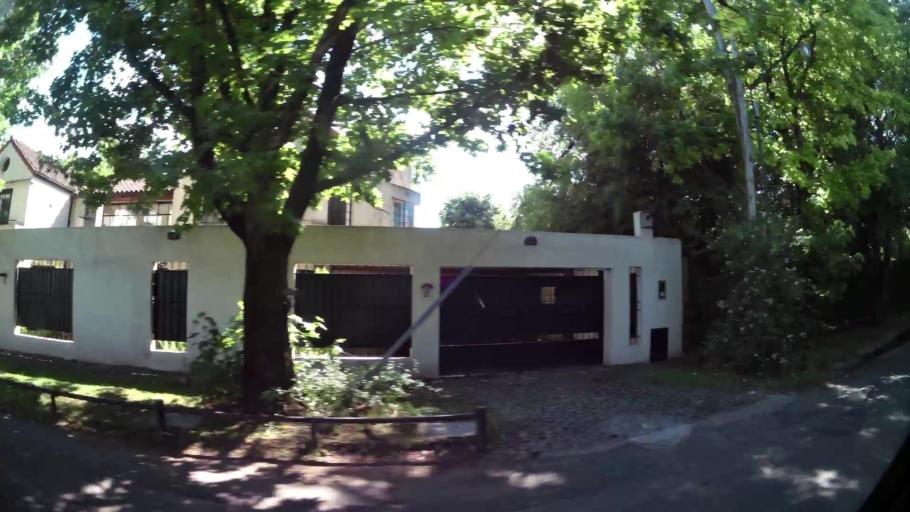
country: AR
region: Buenos Aires
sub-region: Partido de Tigre
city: Tigre
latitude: -34.4852
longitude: -58.5753
